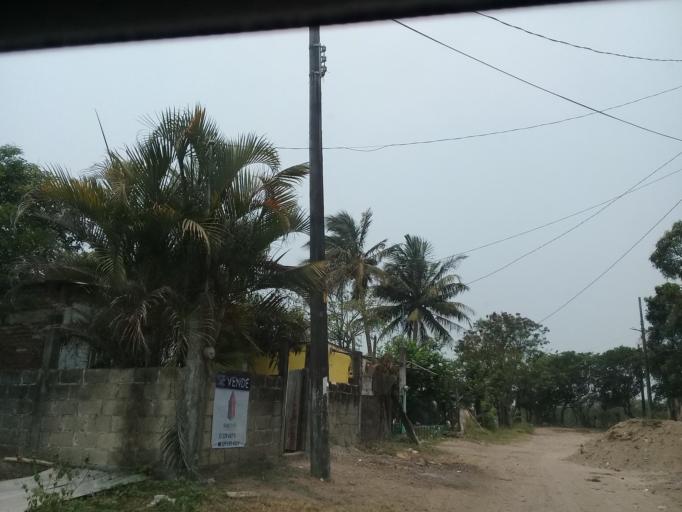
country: MX
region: Veracruz
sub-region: Veracruz
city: Las Amapolas
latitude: 19.1409
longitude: -96.2086
